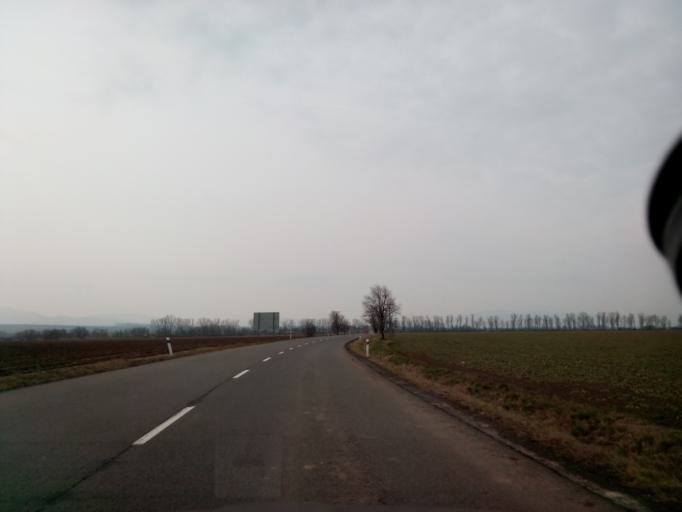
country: SK
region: Kosicky
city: Trebisov
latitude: 48.5497
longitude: 21.6873
